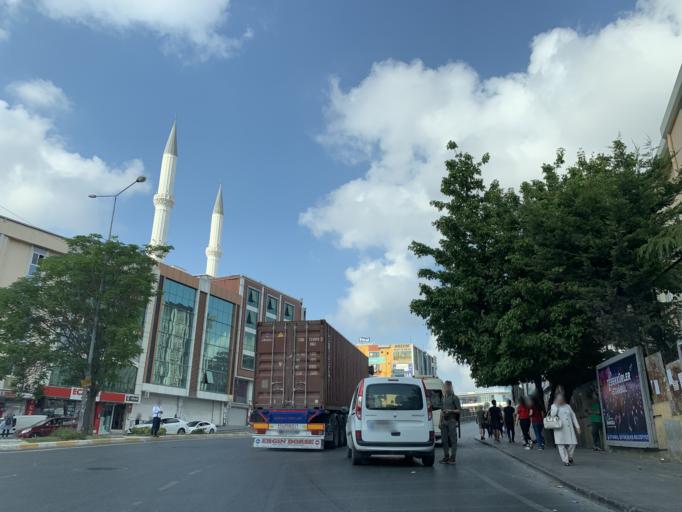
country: TR
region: Istanbul
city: Esenyurt
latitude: 41.0335
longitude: 28.6775
